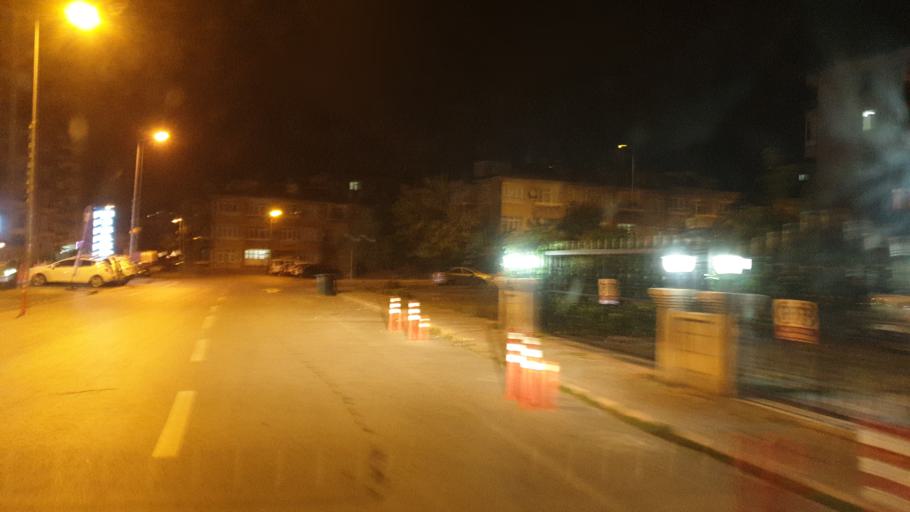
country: TR
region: Kayseri
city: Talas
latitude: 38.6950
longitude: 35.5434
